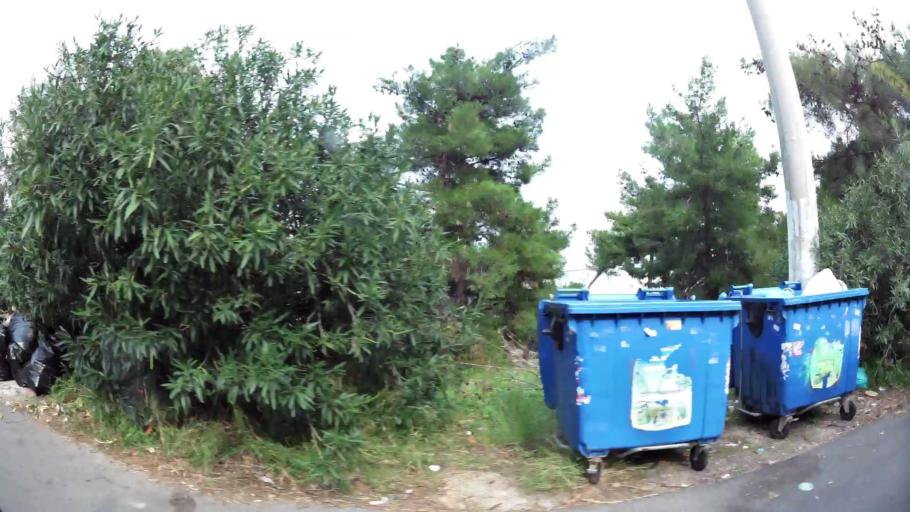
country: GR
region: Attica
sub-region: Nomarchia Athinas
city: Filothei
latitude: 38.0268
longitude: 23.7718
